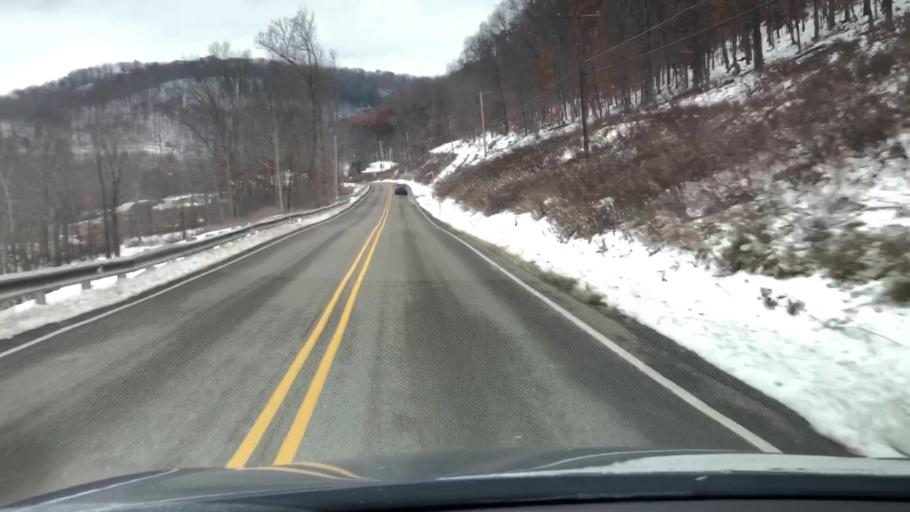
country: US
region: Pennsylvania
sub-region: Elk County
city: Saint Marys
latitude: 41.2780
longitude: -78.4682
